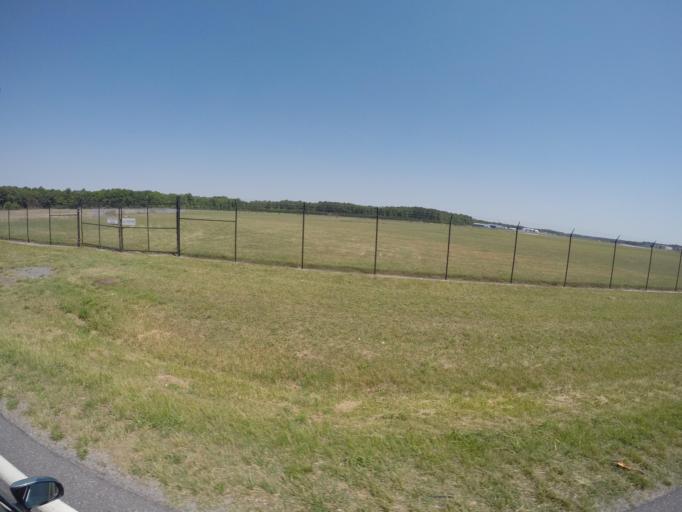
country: US
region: Delaware
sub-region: Sussex County
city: Georgetown
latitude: 38.6812
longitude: -75.3681
